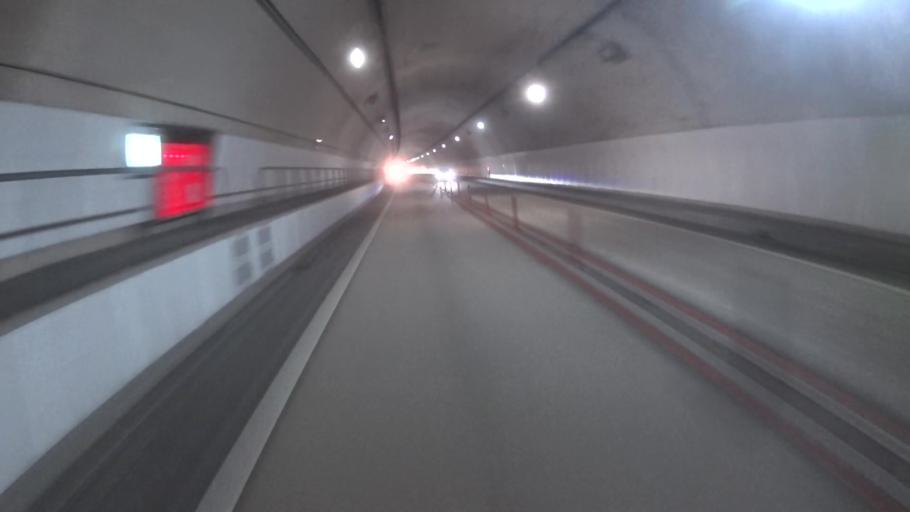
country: JP
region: Kyoto
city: Ayabe
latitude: 35.3059
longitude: 135.3278
